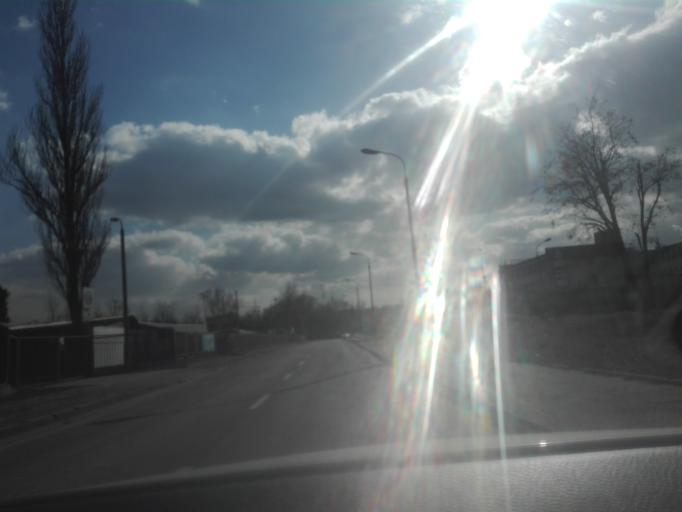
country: PL
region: Silesian Voivodeship
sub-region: Katowice
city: Katowice
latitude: 50.2591
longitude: 18.9953
